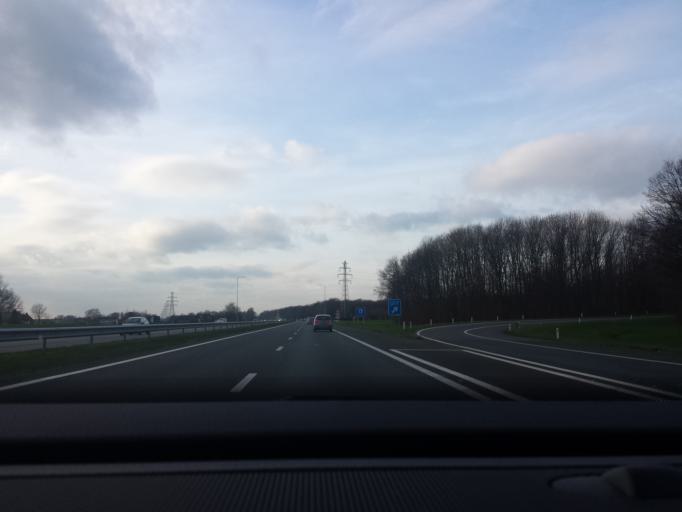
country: NL
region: Gelderland
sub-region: Gemeente Doetinchem
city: Doetinchem
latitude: 51.9448
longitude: 6.2187
